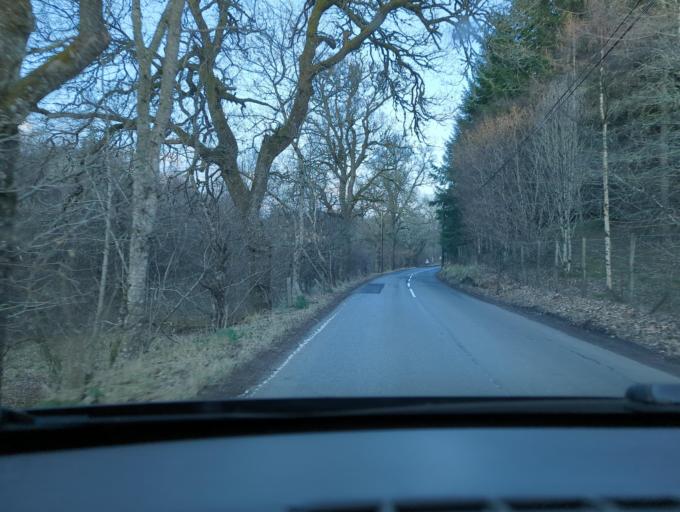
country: GB
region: Scotland
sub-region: Perth and Kinross
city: Methven
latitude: 56.5373
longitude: -3.6713
